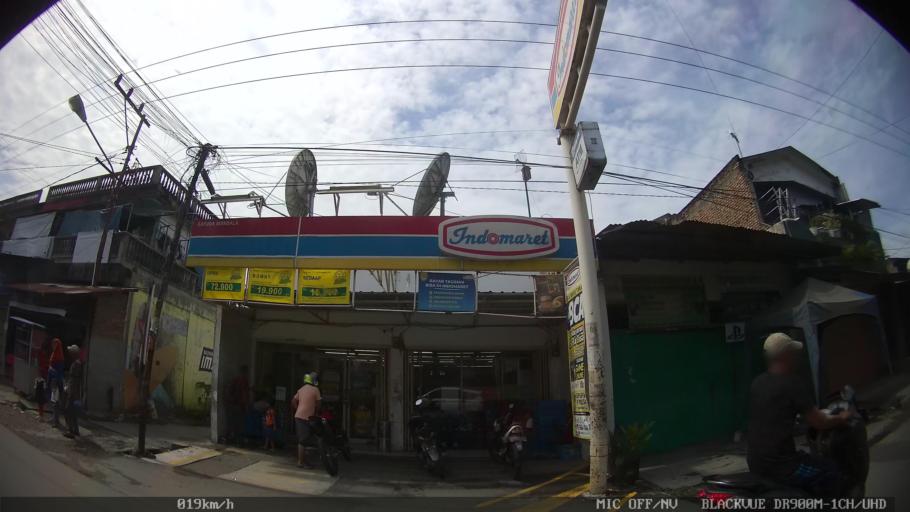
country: ID
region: North Sumatra
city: Medan
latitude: 3.5871
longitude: 98.7200
